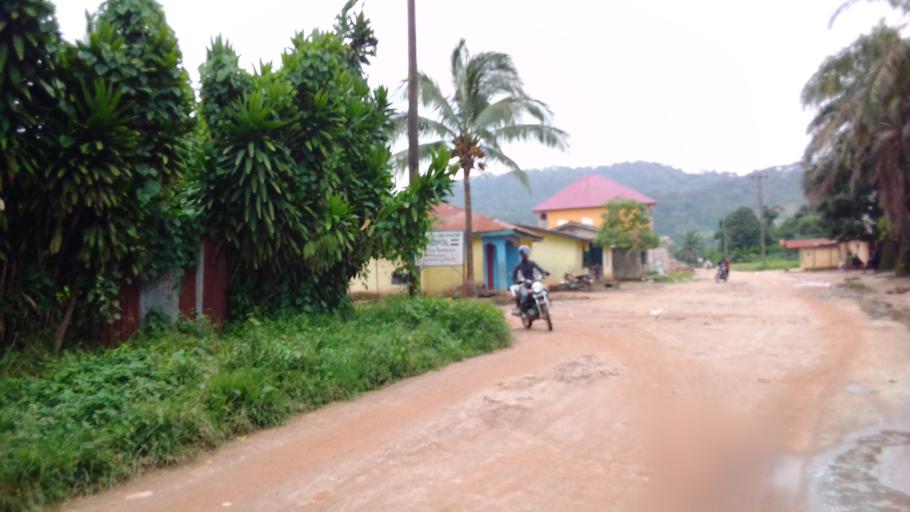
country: SL
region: Eastern Province
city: Kenema
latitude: 7.8693
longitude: -11.1989
